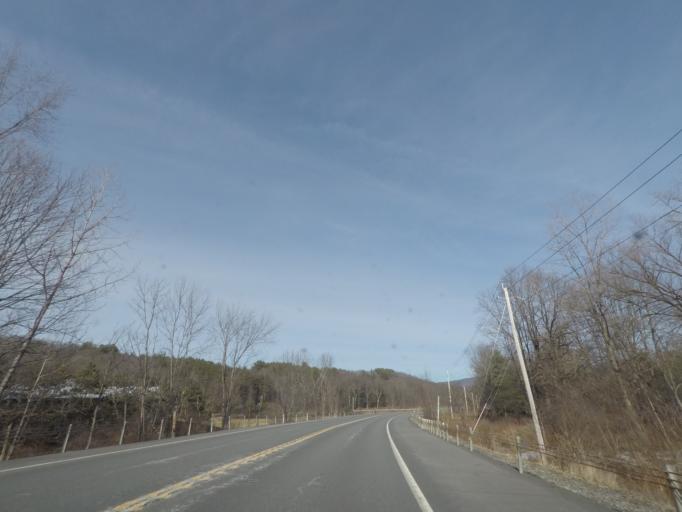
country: US
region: Massachusetts
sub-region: Berkshire County
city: Williamstown
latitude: 42.7400
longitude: -73.3595
